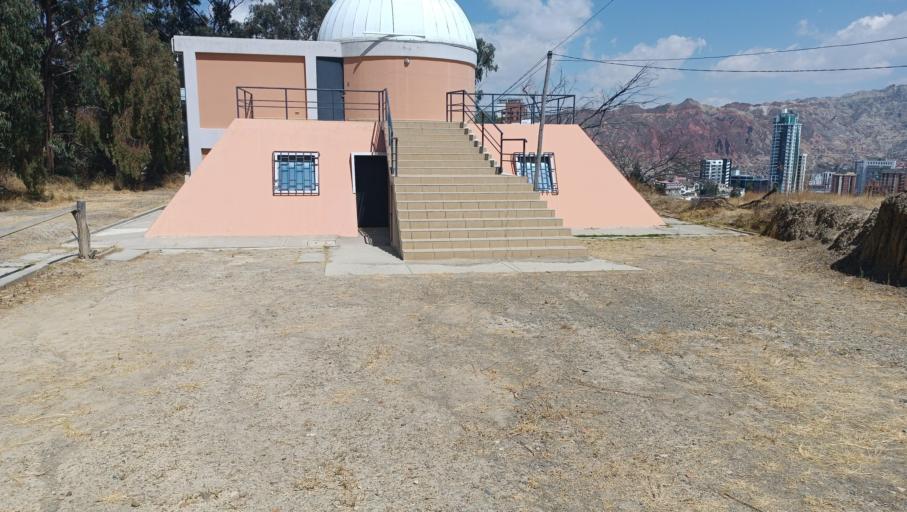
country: BO
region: La Paz
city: La Paz
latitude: -16.5381
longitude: -68.0699
